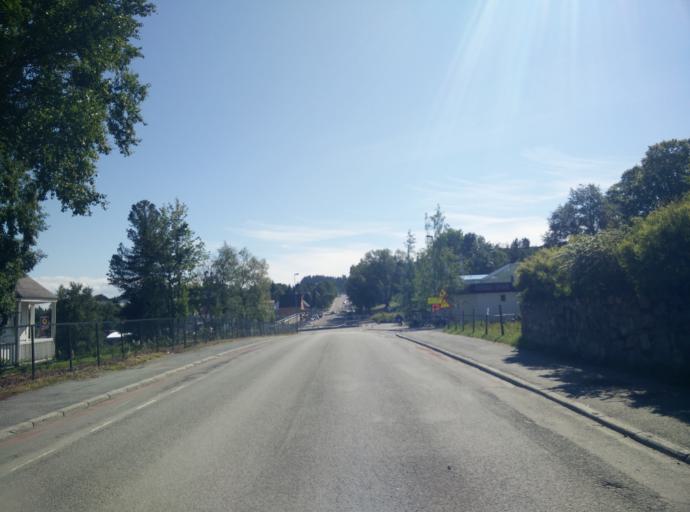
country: NO
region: Sor-Trondelag
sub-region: Trondheim
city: Trondheim
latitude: 63.4186
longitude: 10.3540
